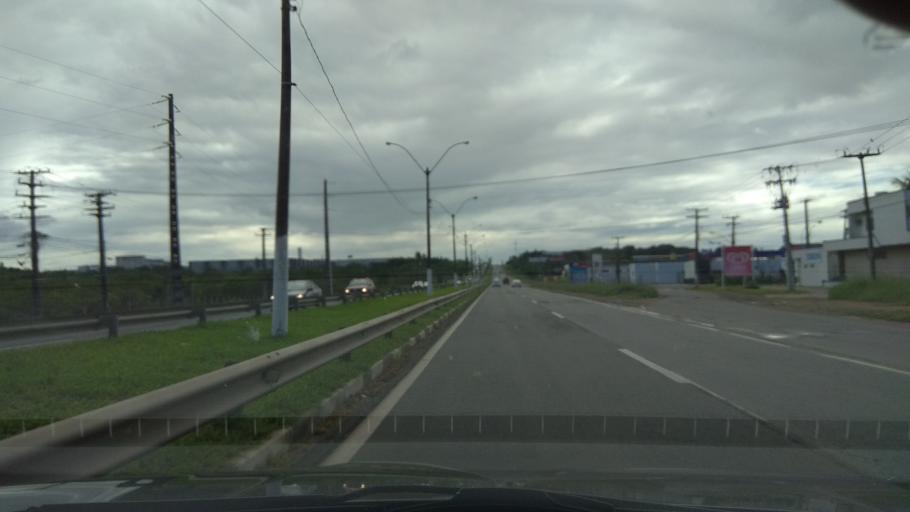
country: BR
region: Bahia
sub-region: Feira De Santana
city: Feira de Santana
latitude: -12.2878
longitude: -38.9149
